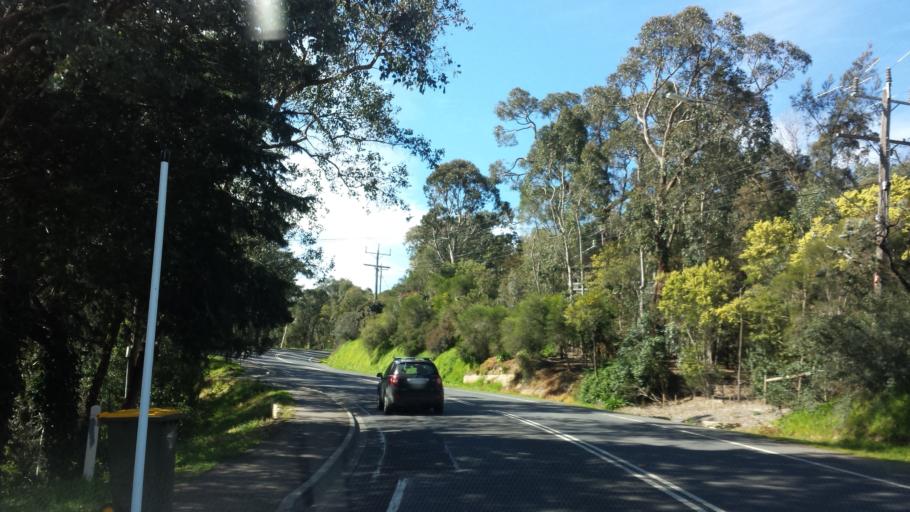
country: AU
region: Victoria
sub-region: Nillumbik
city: North Warrandyte
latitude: -37.7342
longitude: 145.2239
